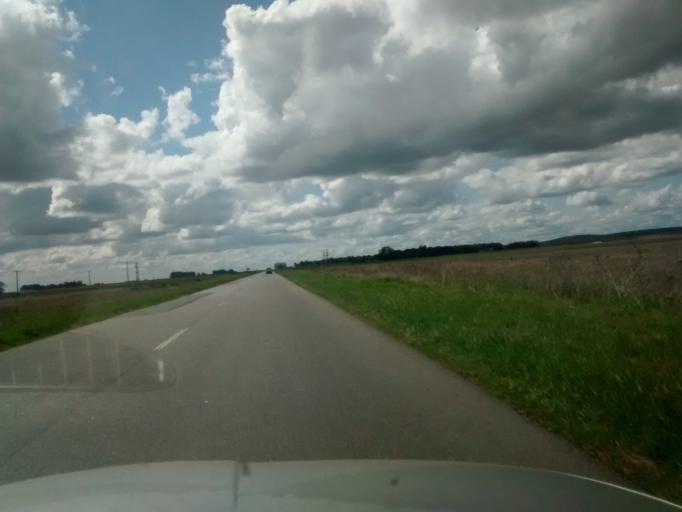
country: AR
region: Buenos Aires
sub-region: Partido de Loberia
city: Loberia
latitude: -37.7035
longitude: -58.7248
